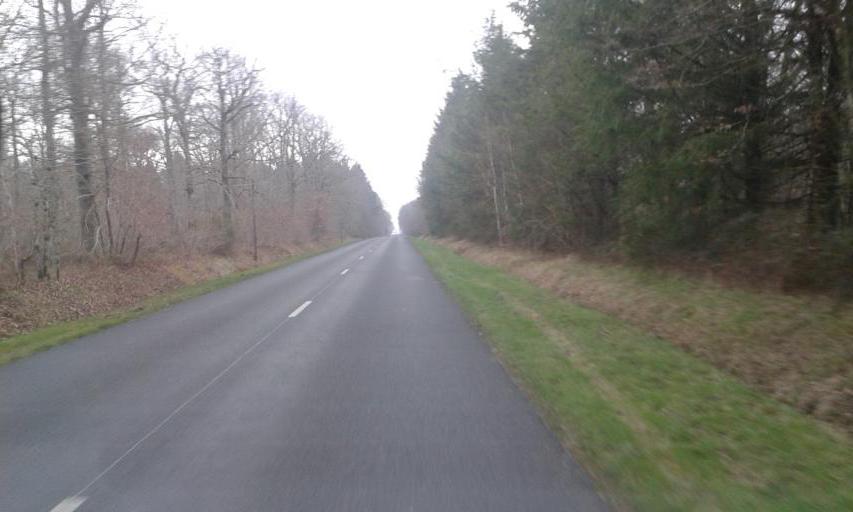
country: FR
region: Centre
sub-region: Departement du Loir-et-Cher
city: Dhuizon
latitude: 47.6674
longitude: 1.6691
